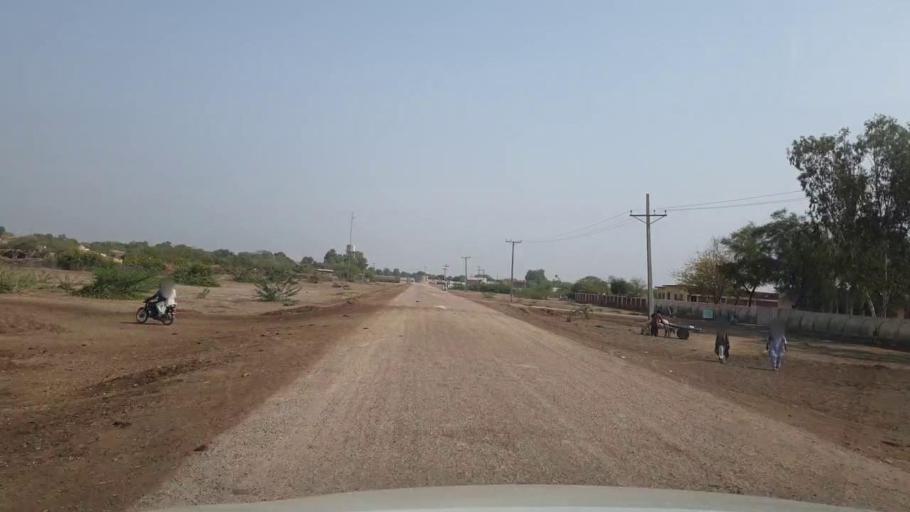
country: PK
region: Sindh
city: Chor
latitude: 25.4500
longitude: 69.7126
